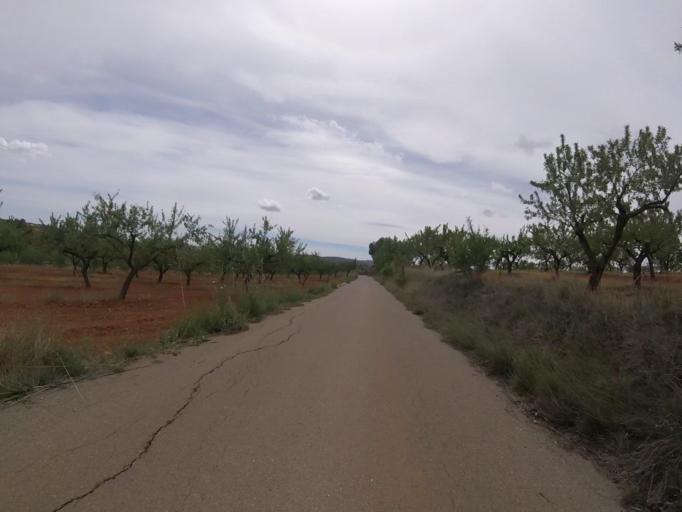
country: ES
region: Valencia
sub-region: Provincia de Castello
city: Benlloch
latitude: 40.1827
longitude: -0.0082
